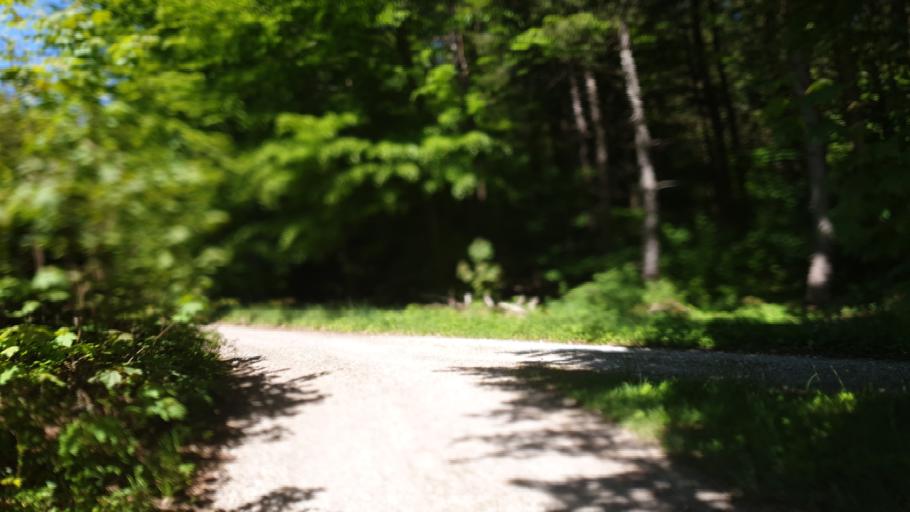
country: DE
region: Bavaria
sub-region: Upper Bavaria
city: Seeshaupt
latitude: 47.8007
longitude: 11.2887
